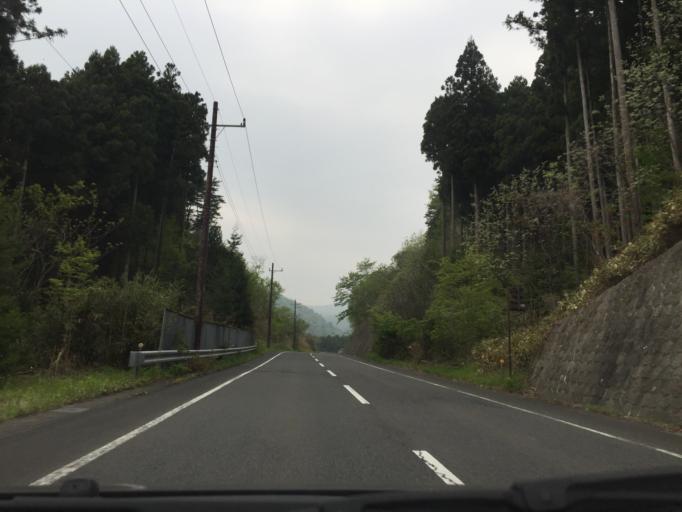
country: JP
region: Tochigi
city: Imaichi
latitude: 36.8609
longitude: 139.7224
